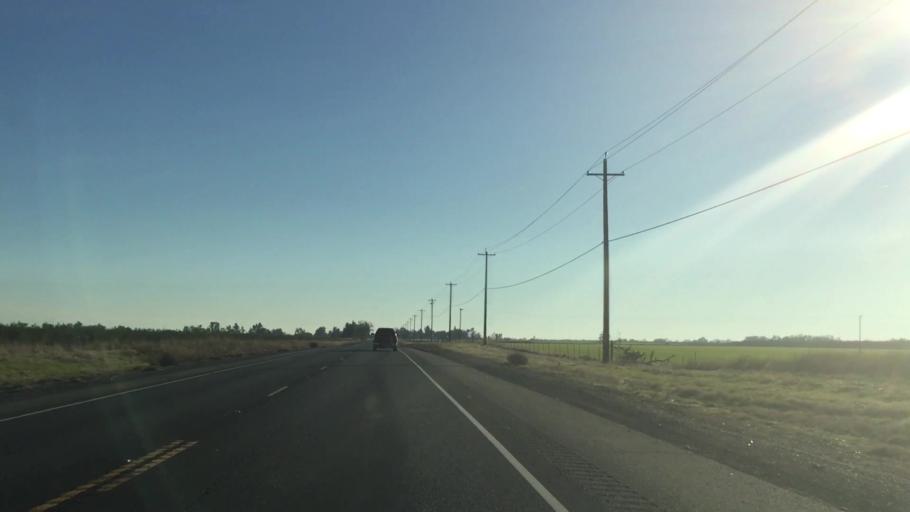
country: US
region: California
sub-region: Butte County
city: Palermo
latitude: 39.4228
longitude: -121.6052
